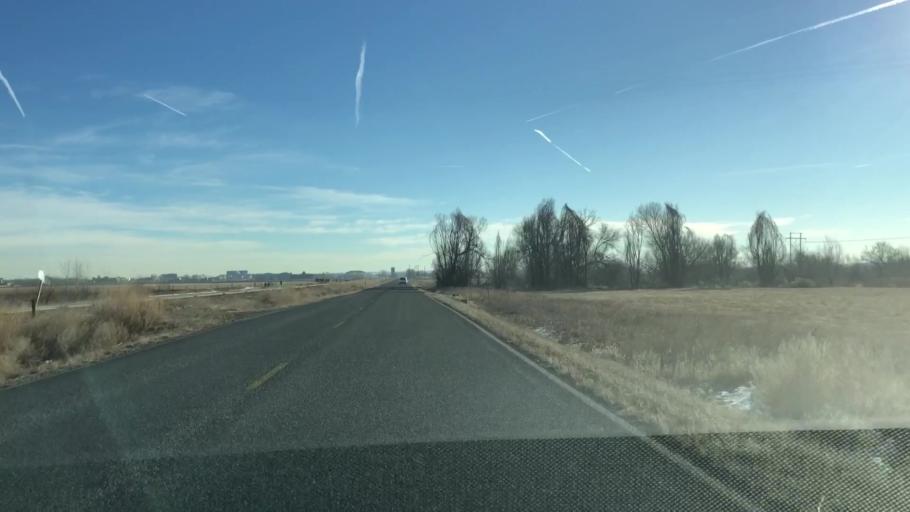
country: US
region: Colorado
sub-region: Larimer County
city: Loveland
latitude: 40.3998
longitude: -105.0137
